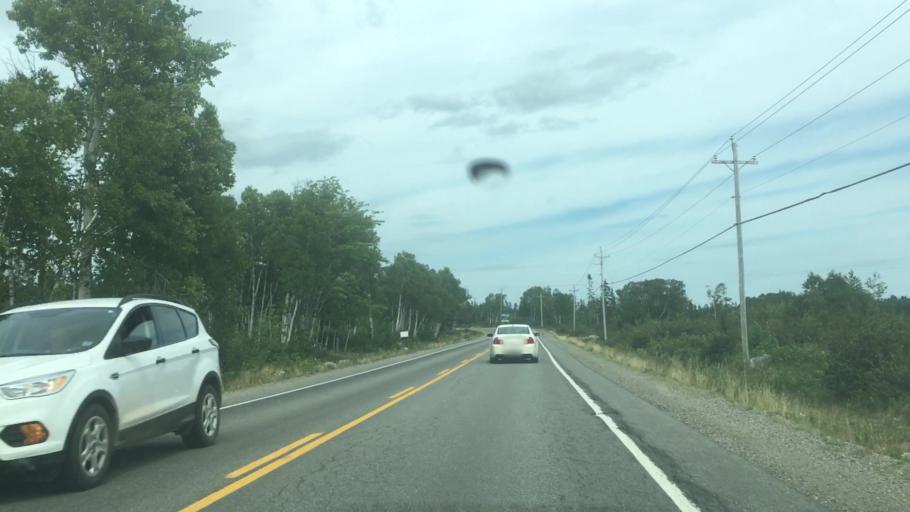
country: CA
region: Nova Scotia
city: Sydney Mines
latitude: 46.5165
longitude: -60.4263
